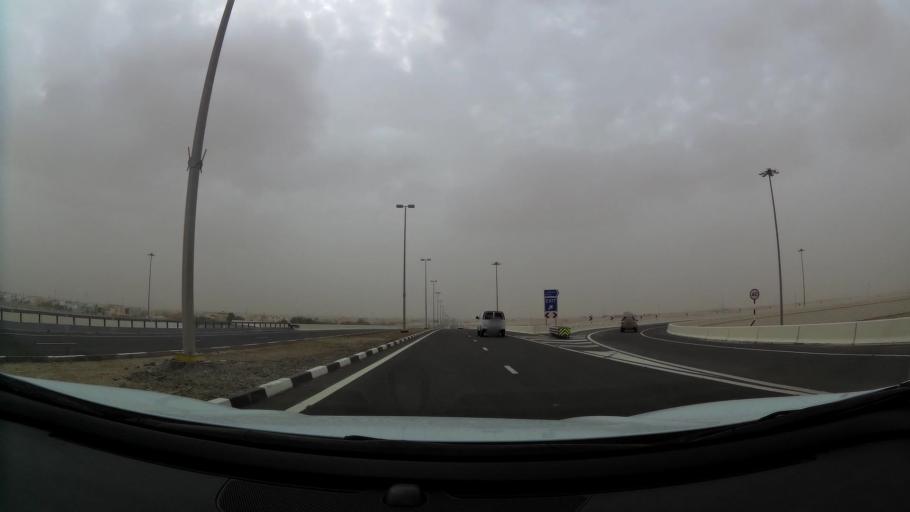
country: AE
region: Abu Dhabi
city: Abu Dhabi
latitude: 24.4130
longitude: 54.7149
